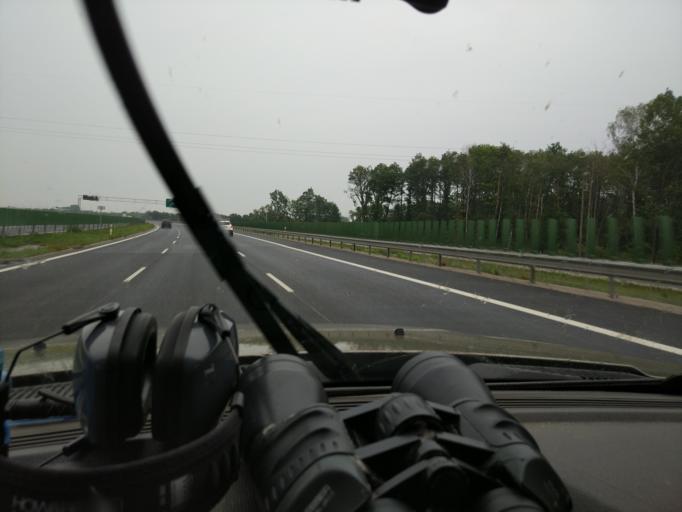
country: PL
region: Masovian Voivodeship
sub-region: Powiat wolominski
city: Kobylka
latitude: 52.3617
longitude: 21.1878
